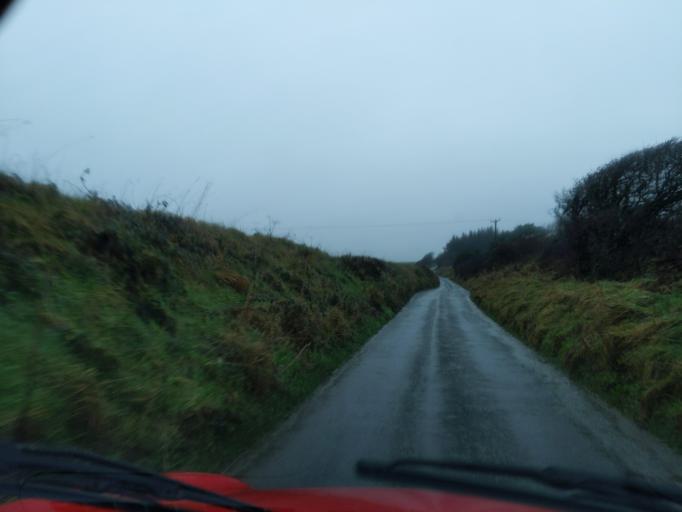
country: GB
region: England
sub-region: Cornwall
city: Camelford
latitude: 50.6471
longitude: -4.6992
